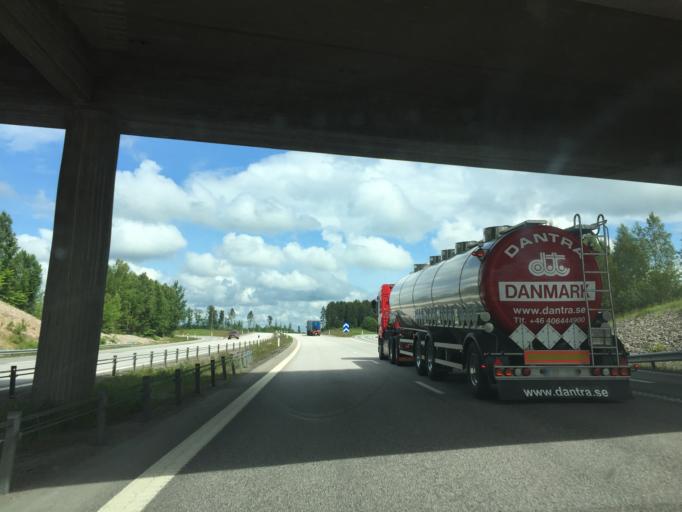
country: SE
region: Vaestmanland
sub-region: Arboga Kommun
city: Arboga
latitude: 59.4122
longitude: 15.7688
